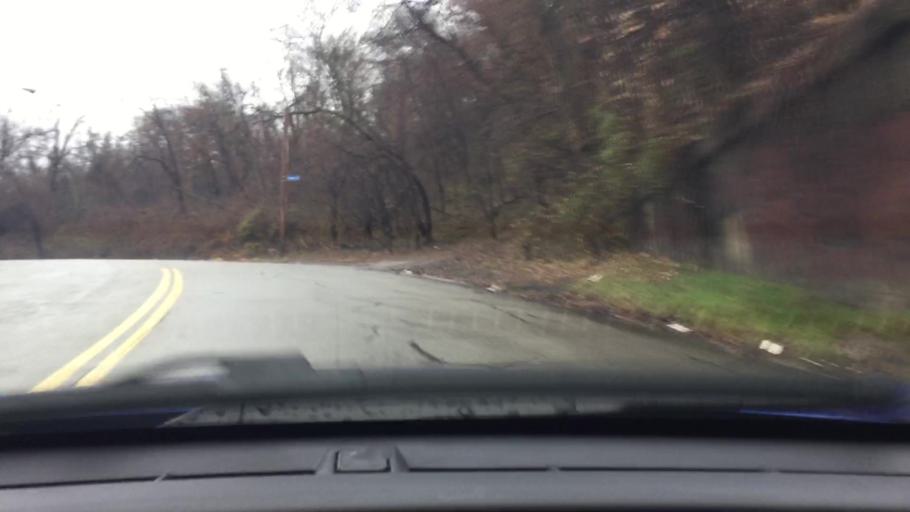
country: US
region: Pennsylvania
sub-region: Allegheny County
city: Pittsburgh
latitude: 40.4395
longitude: -79.9730
